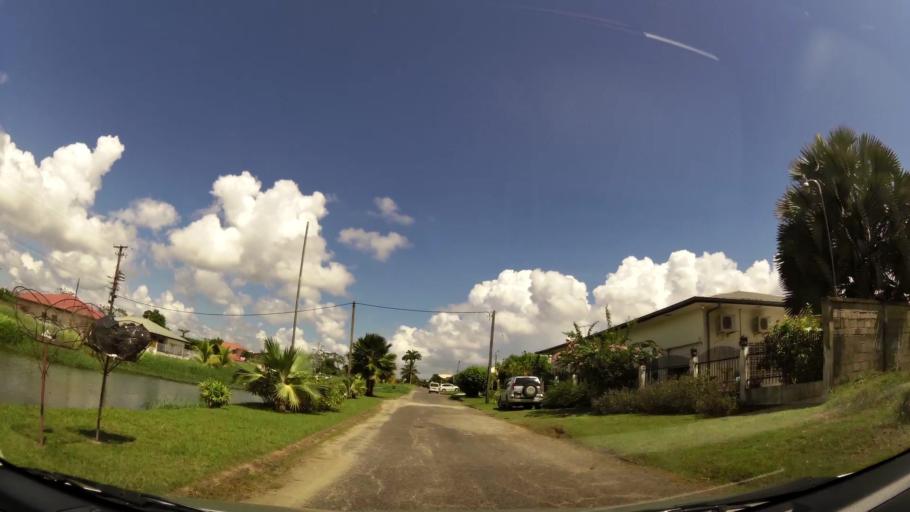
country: SR
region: Paramaribo
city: Paramaribo
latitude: 5.8599
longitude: -55.1299
